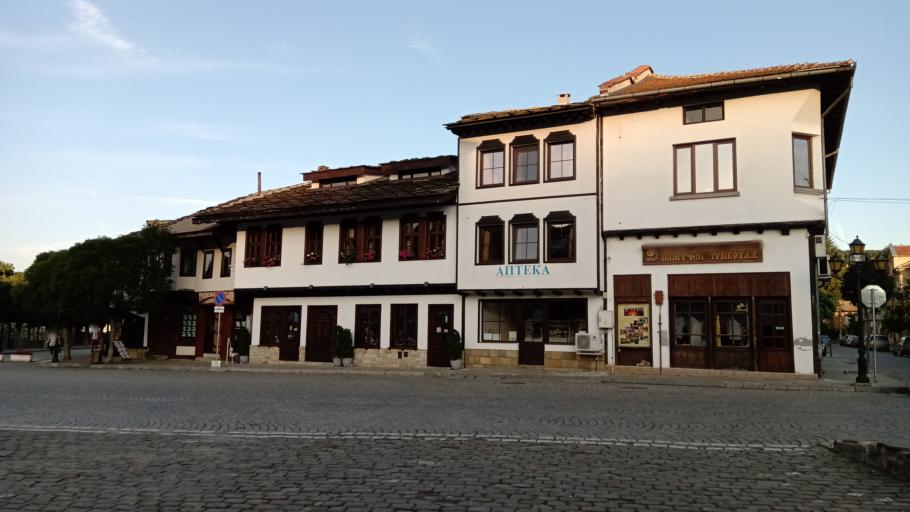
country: BG
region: Gabrovo
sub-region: Obshtina Tryavna
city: Tryavna
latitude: 42.8661
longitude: 25.4897
